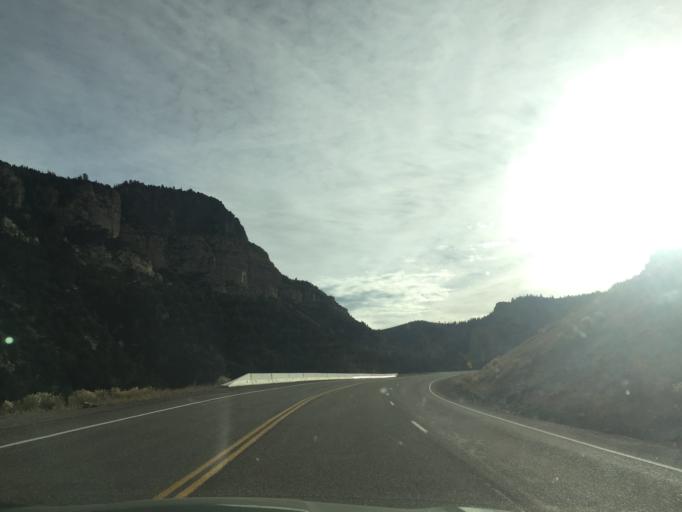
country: US
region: Utah
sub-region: Iron County
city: Cedar City
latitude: 37.6354
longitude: -112.9474
